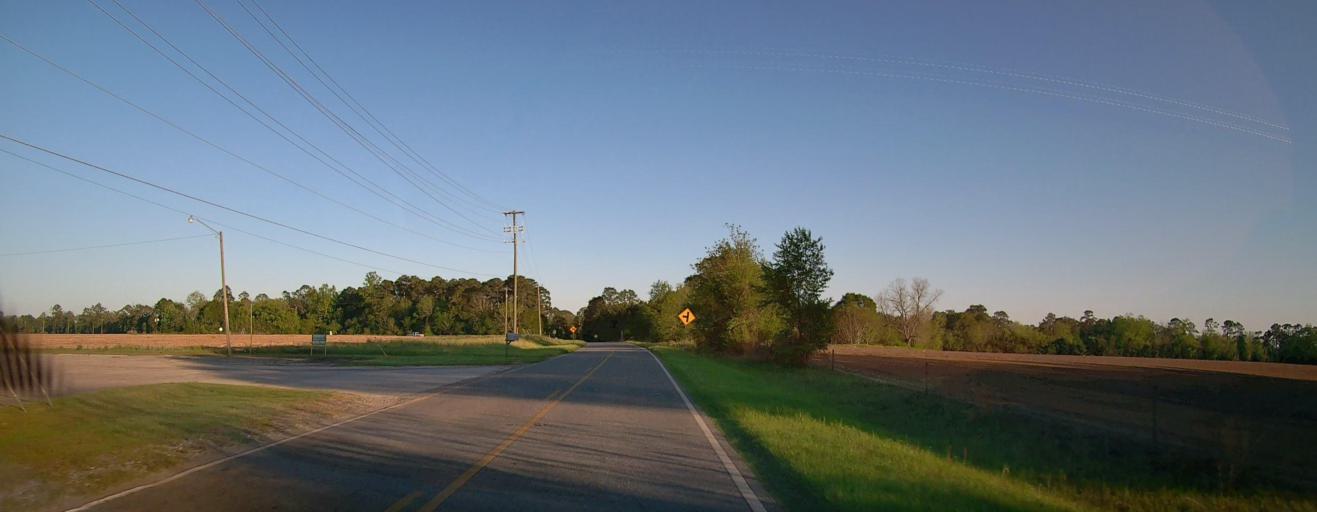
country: US
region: Georgia
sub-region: Ben Hill County
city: Fitzgerald
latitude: 31.6934
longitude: -83.2352
